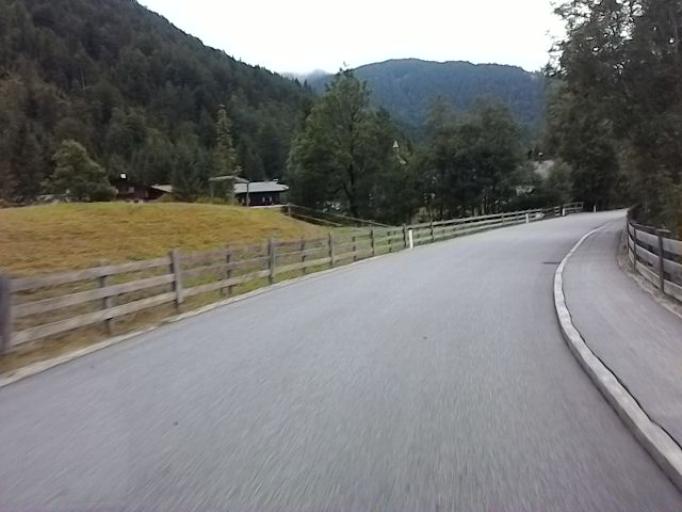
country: DE
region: Bavaria
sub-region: Upper Bavaria
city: Jachenau
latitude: 47.4702
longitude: 11.4698
